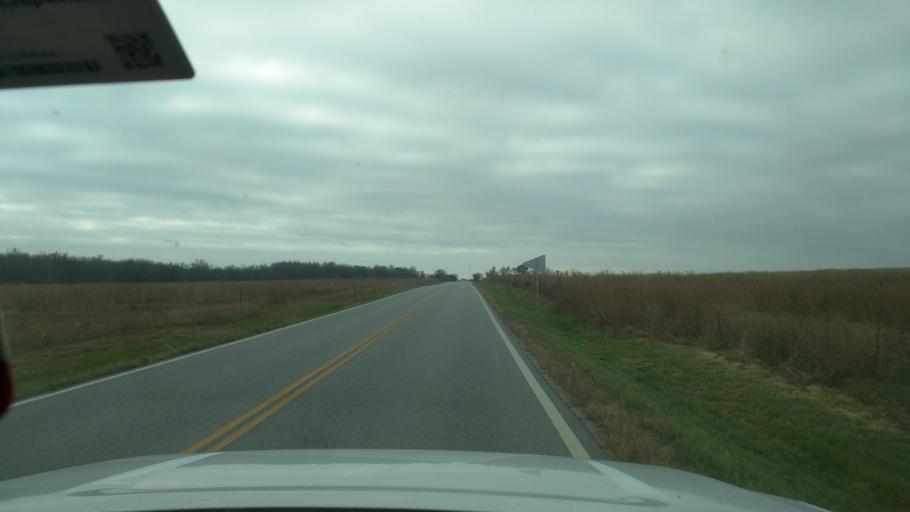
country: US
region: Kansas
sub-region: Greenwood County
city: Eureka
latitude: 37.6631
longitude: -96.2345
